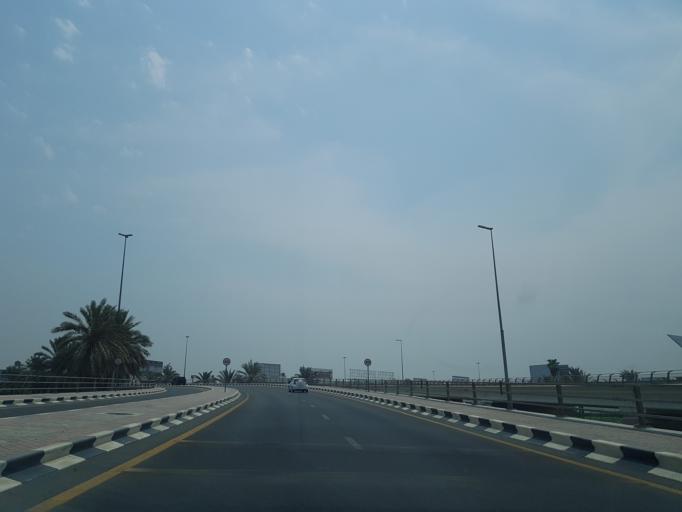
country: AE
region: Ash Shariqah
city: Sharjah
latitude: 25.2495
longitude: 55.3345
